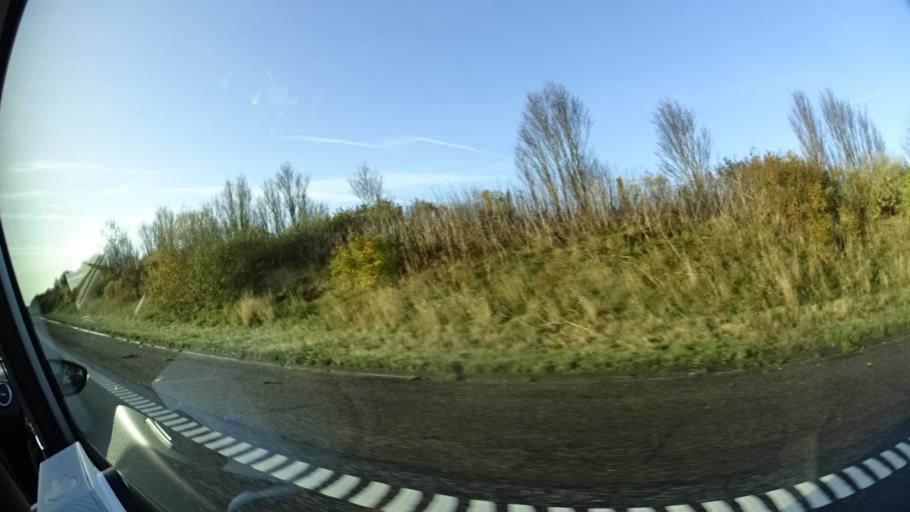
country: DK
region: South Denmark
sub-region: Fredericia Kommune
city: Taulov
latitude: 55.5831
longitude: 9.6108
